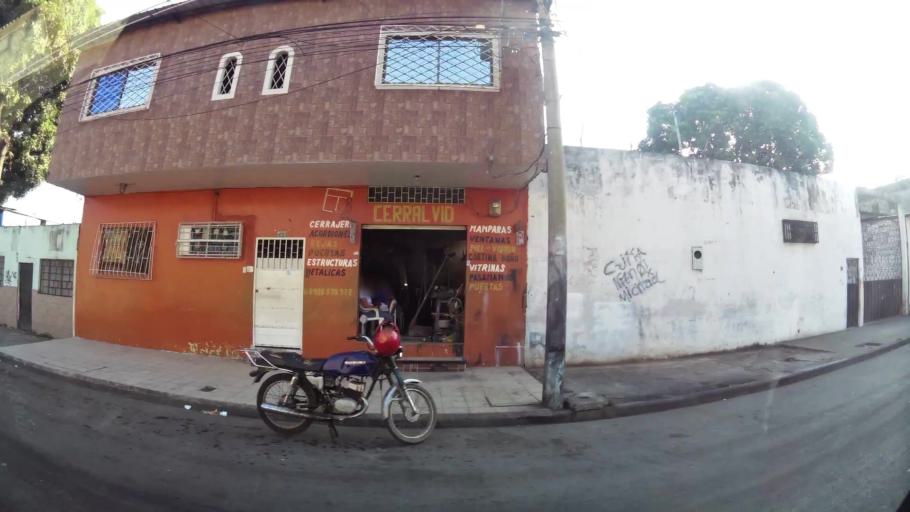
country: EC
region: Guayas
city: Eloy Alfaro
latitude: -2.1765
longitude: -79.8542
